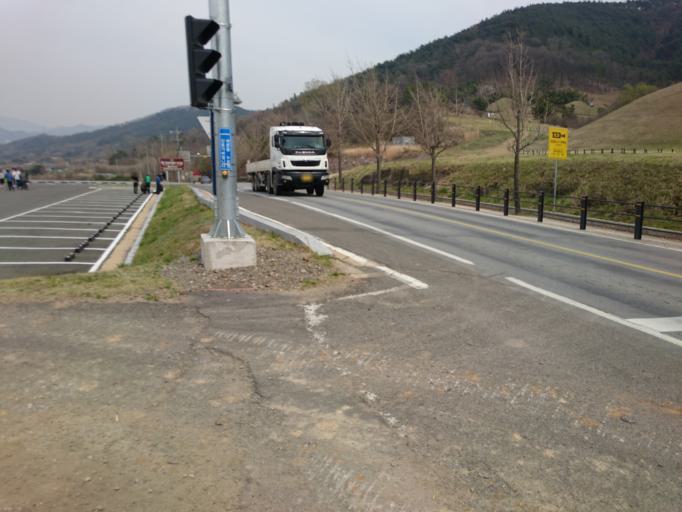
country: KR
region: Gyeongsangnam-do
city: Changnyeong
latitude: 35.5464
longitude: 128.5049
